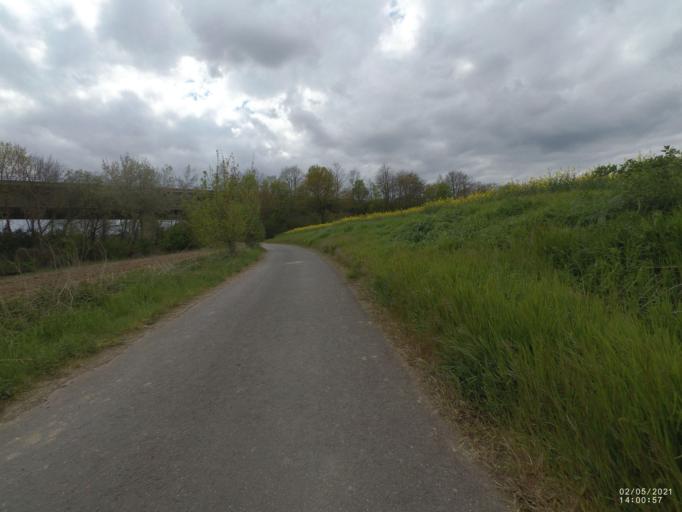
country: DE
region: Rheinland-Pfalz
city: Bassenheim
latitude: 50.3669
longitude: 7.4687
